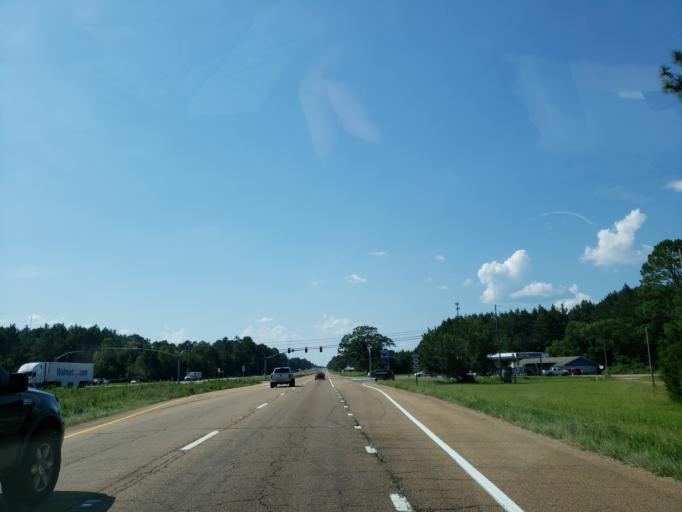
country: US
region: Mississippi
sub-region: Covington County
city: Collins
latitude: 31.5613
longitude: -89.5110
